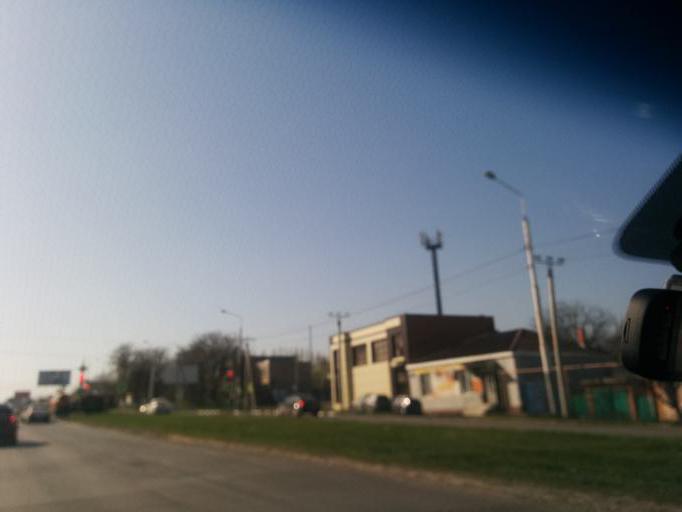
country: RU
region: Rostov
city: Shakhty
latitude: 47.7109
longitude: 40.1650
